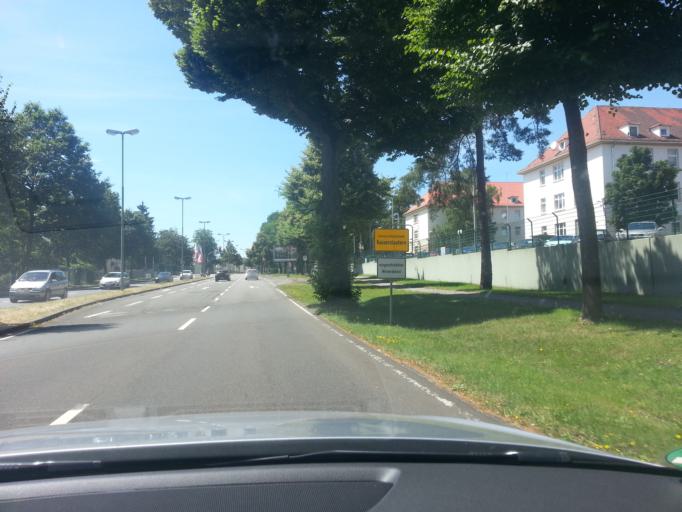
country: DE
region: Rheinland-Pfalz
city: Kaiserslautern
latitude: 49.4435
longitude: 7.8125
